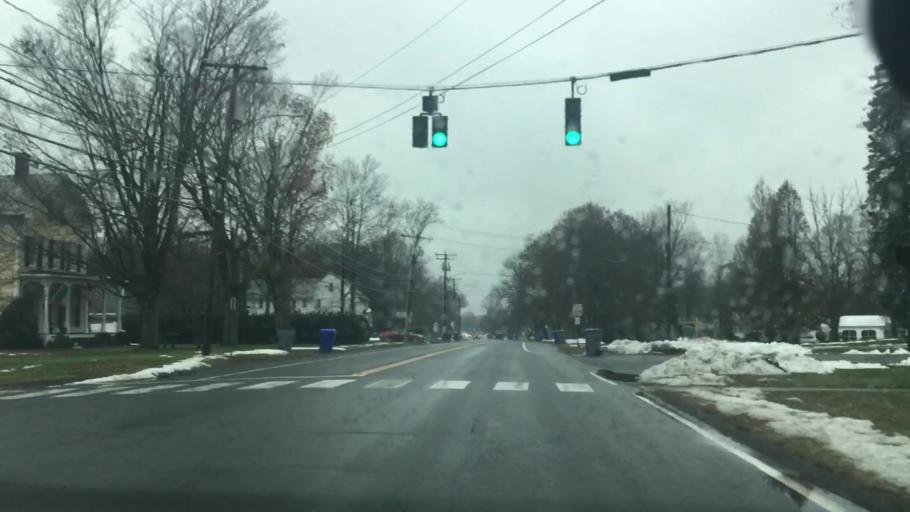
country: US
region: Connecticut
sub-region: Hartford County
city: Enfield
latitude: 41.9719
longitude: -72.5926
